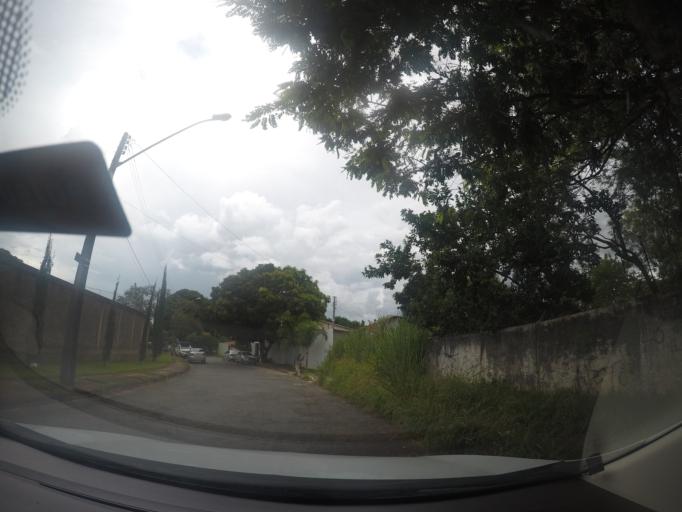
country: BR
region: Goias
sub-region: Goiania
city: Goiania
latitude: -16.6491
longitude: -49.2388
